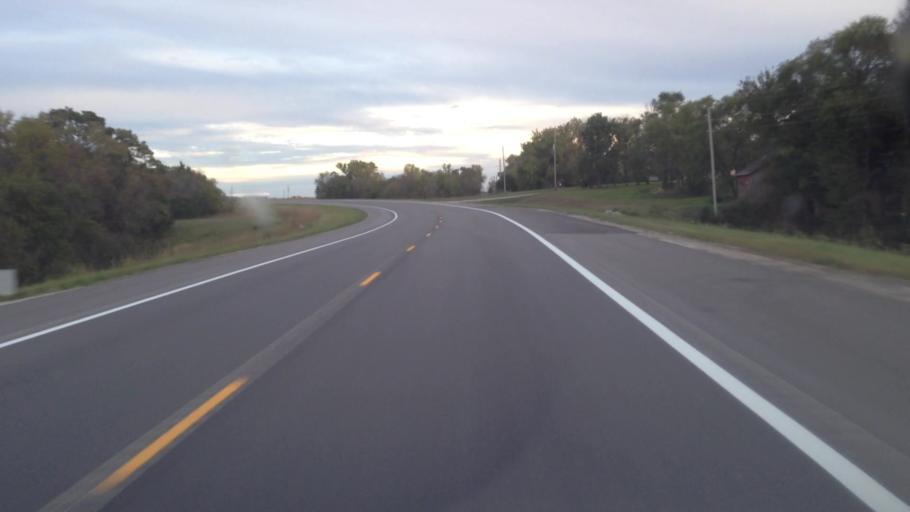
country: US
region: Kansas
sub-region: Franklin County
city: Ottawa
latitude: 38.4762
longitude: -95.2674
